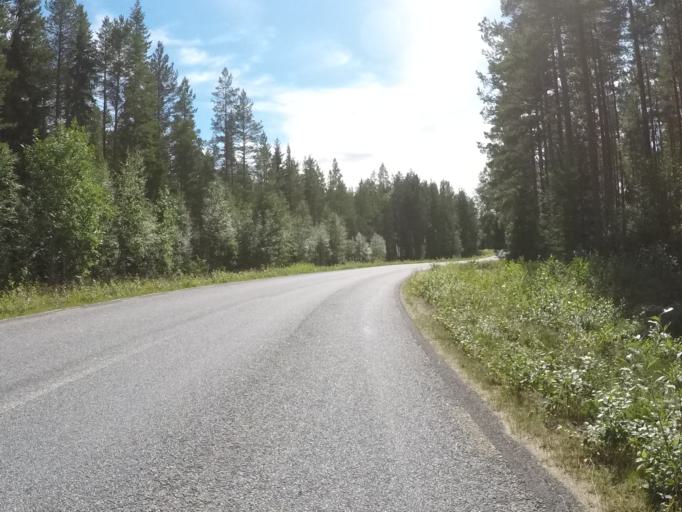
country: SE
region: Vaesterbotten
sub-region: Robertsfors Kommun
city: Robertsfors
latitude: 63.9786
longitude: 20.8106
